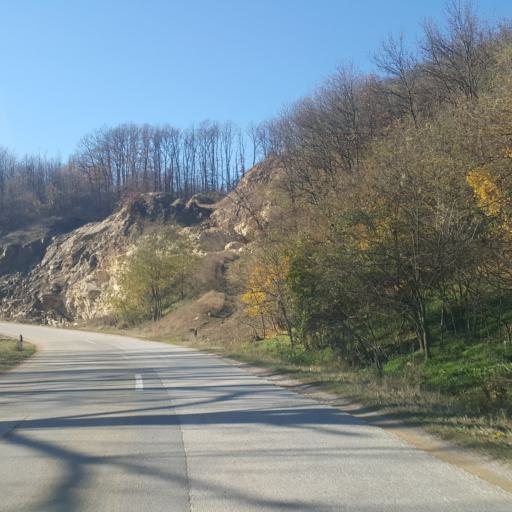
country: RS
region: Central Serbia
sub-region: Sumadijski Okrug
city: Raca
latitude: 44.2460
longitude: 20.8903
